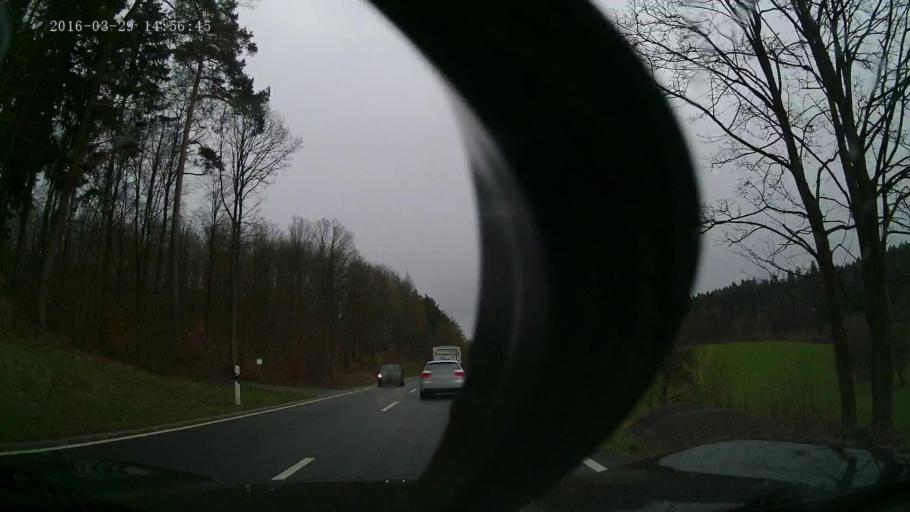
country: DE
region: Baden-Wuerttemberg
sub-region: Karlsruhe Region
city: Walldurn
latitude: 49.5980
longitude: 9.3569
